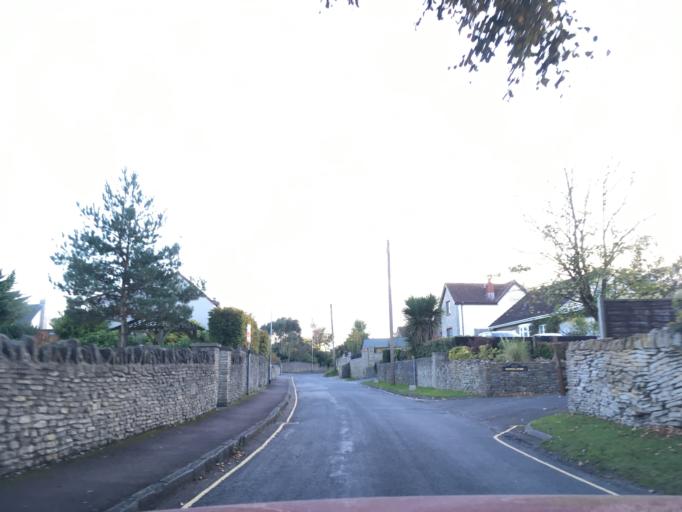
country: GB
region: England
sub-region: South Gloucestershire
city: Stoke Gifford
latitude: 51.5085
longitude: -2.5471
